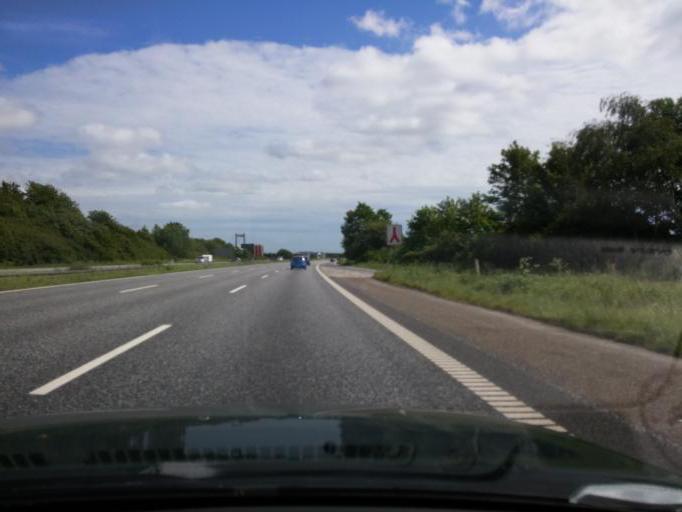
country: DK
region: South Denmark
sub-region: Fredericia Kommune
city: Snoghoj
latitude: 55.5310
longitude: 9.7201
